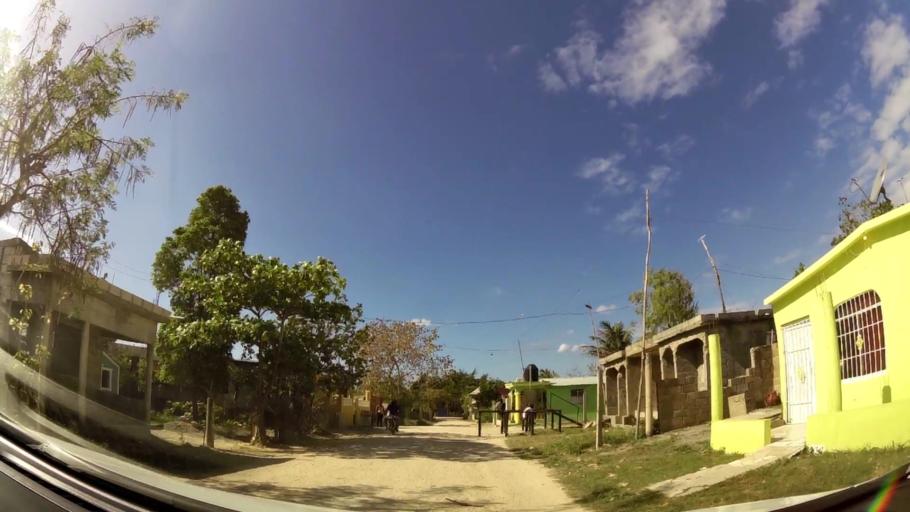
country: DO
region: Santo Domingo
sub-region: Santo Domingo
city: Boca Chica
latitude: 18.4604
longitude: -69.6030
